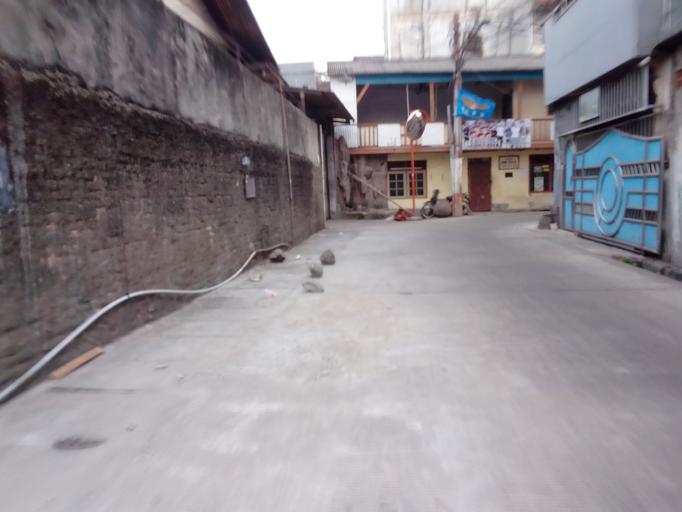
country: ID
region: Jakarta Raya
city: Jakarta
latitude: -6.1641
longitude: 106.8068
